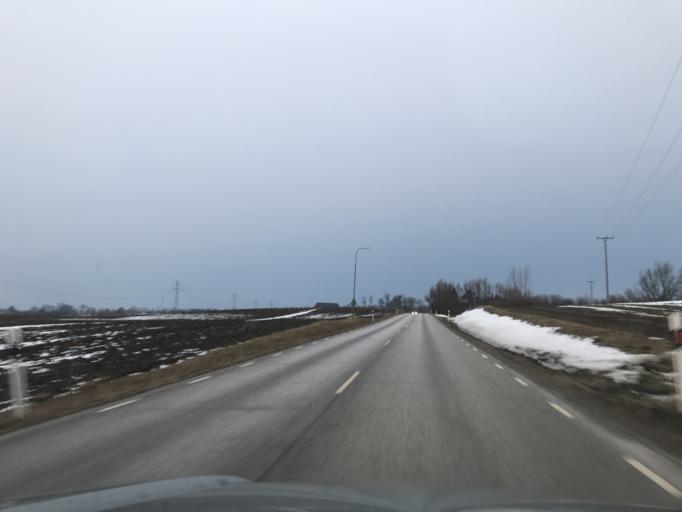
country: SE
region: Skane
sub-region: Malmo
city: Oxie
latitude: 55.5179
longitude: 13.0869
